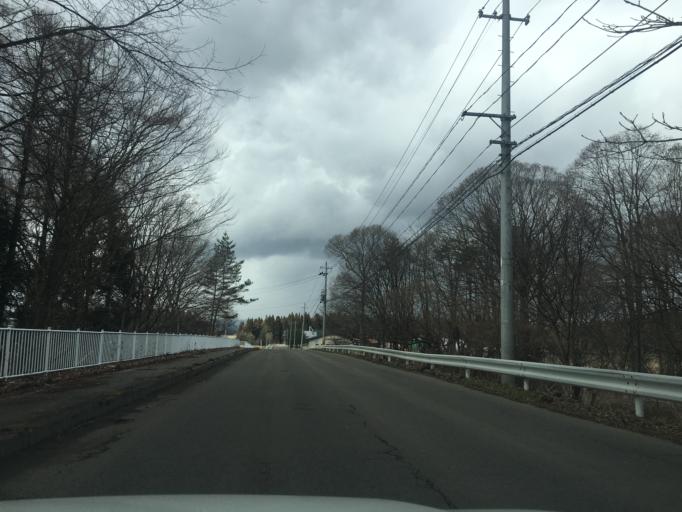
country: JP
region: Akita
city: Takanosu
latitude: 40.1826
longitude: 140.3426
